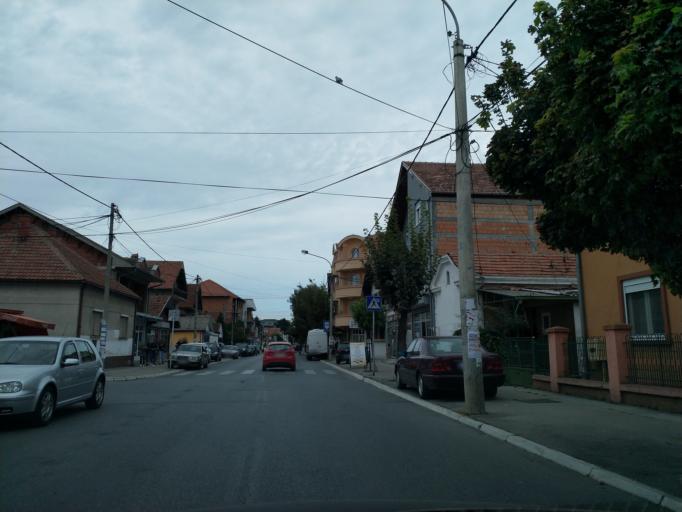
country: RS
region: Central Serbia
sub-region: Pomoravski Okrug
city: Jagodina
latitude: 43.9825
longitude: 21.2544
